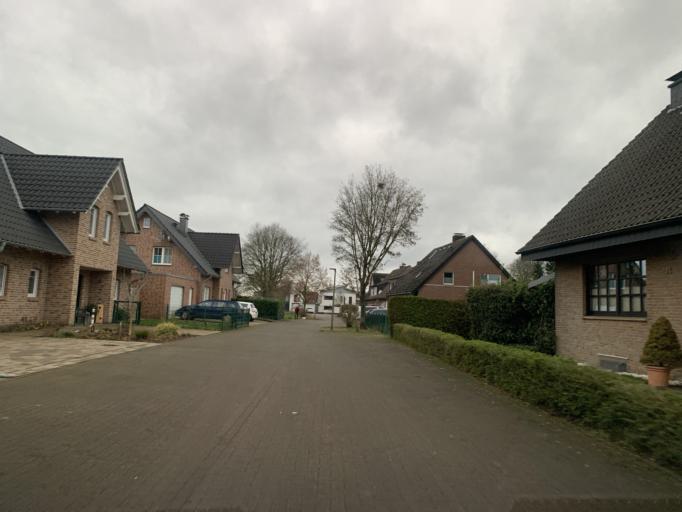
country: DE
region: North Rhine-Westphalia
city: Olfen
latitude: 51.7329
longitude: 7.2932
